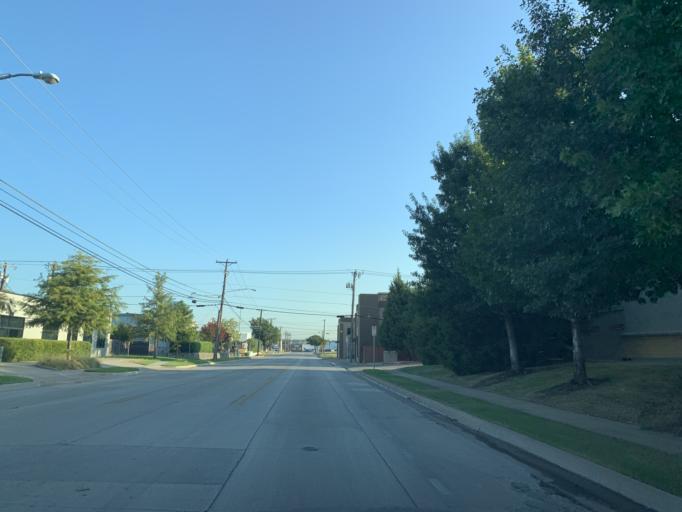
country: US
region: Texas
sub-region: Tarrant County
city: River Oaks
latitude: 32.7561
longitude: -97.3546
